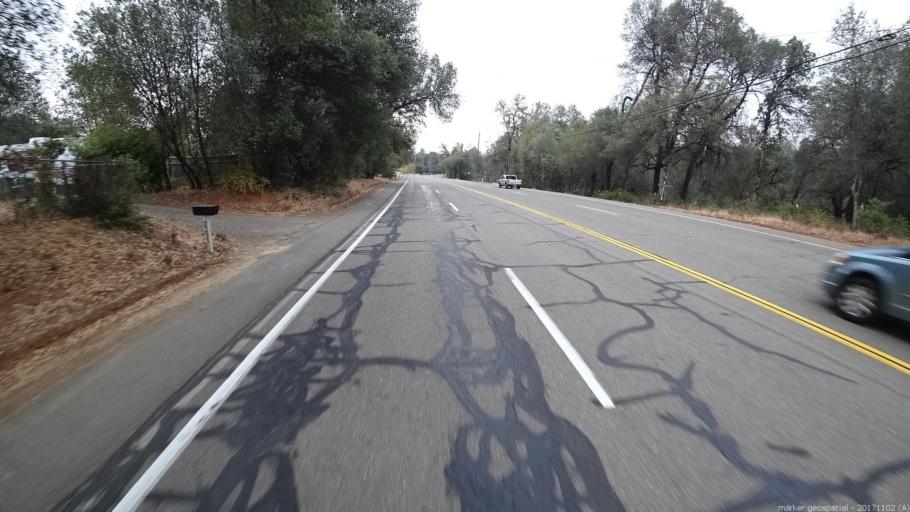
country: US
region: California
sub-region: Shasta County
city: Central Valley (historical)
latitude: 40.6466
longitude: -122.3978
